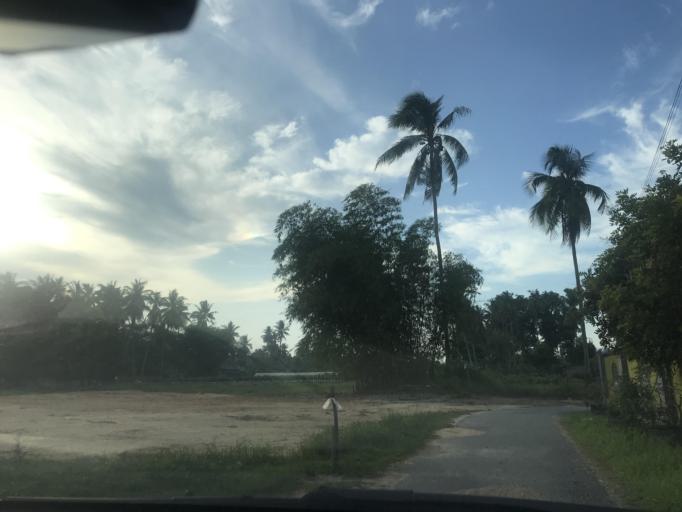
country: MY
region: Kelantan
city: Peringat
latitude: 6.1191
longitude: 102.3550
